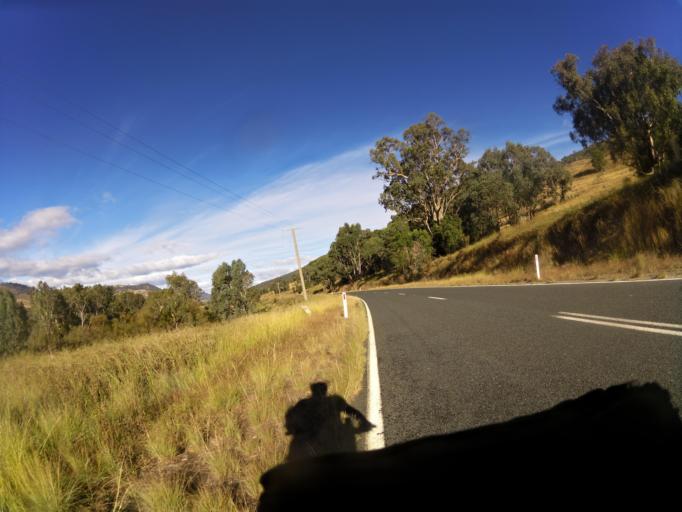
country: AU
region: New South Wales
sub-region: Greater Hume Shire
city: Holbrook
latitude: -35.9687
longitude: 147.7754
